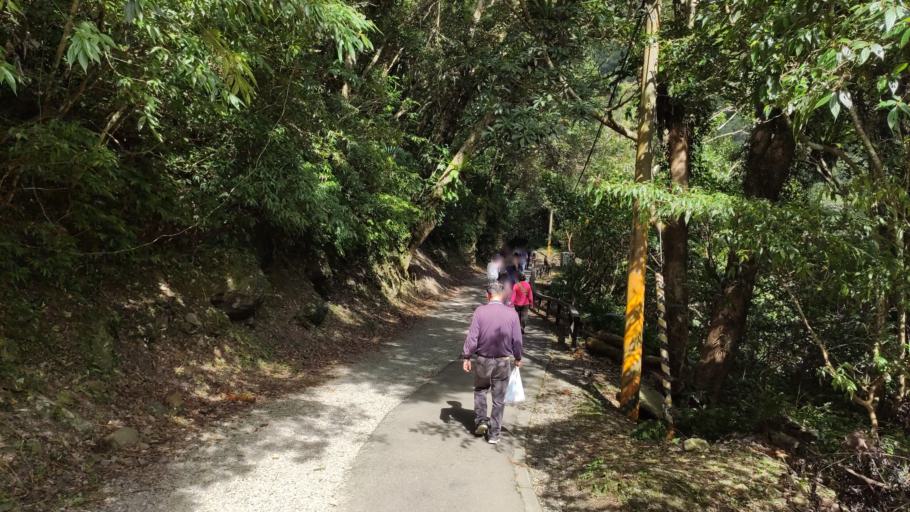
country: TW
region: Taiwan
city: Daxi
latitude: 24.8226
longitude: 121.4489
